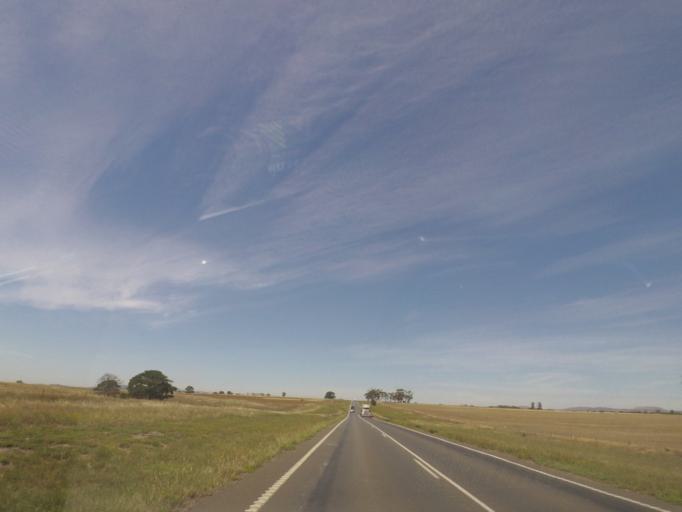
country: AU
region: Victoria
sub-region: Moorabool
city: Bacchus Marsh
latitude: -37.8095
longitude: 144.4015
